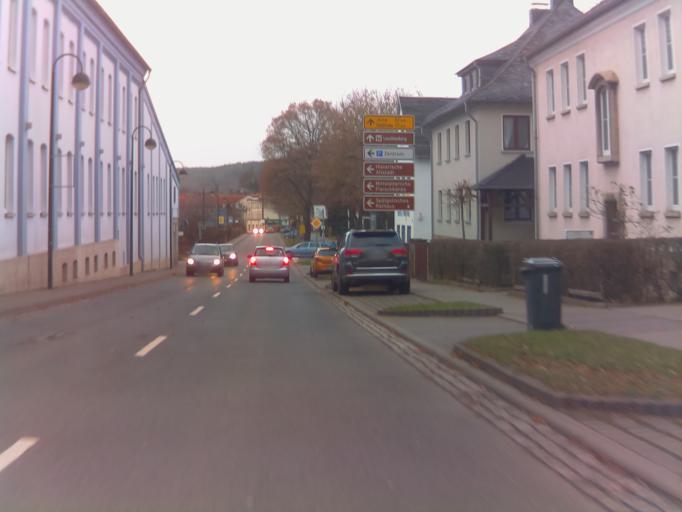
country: DE
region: Thuringia
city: Neustadt (Orla)
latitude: 50.7361
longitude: 11.7532
